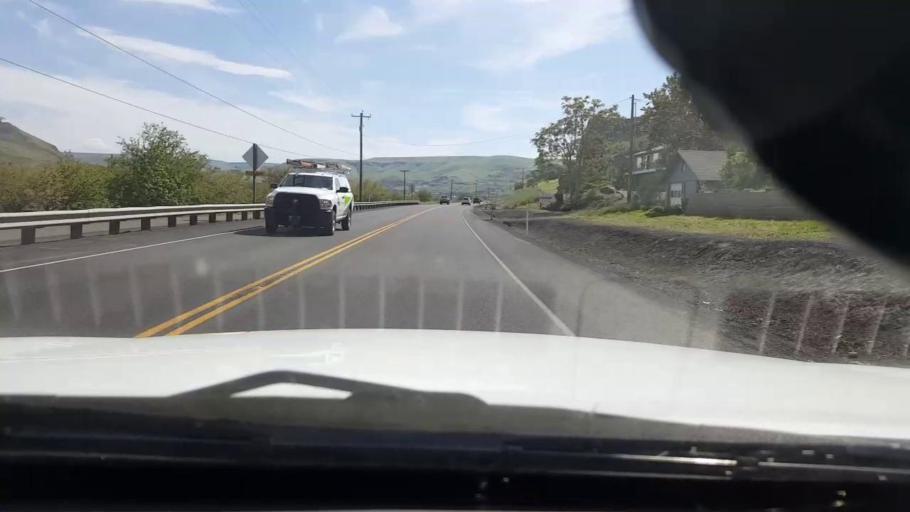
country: US
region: Washington
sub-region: Asotin County
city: West Clarkston-Highland
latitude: 46.3792
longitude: -117.0519
